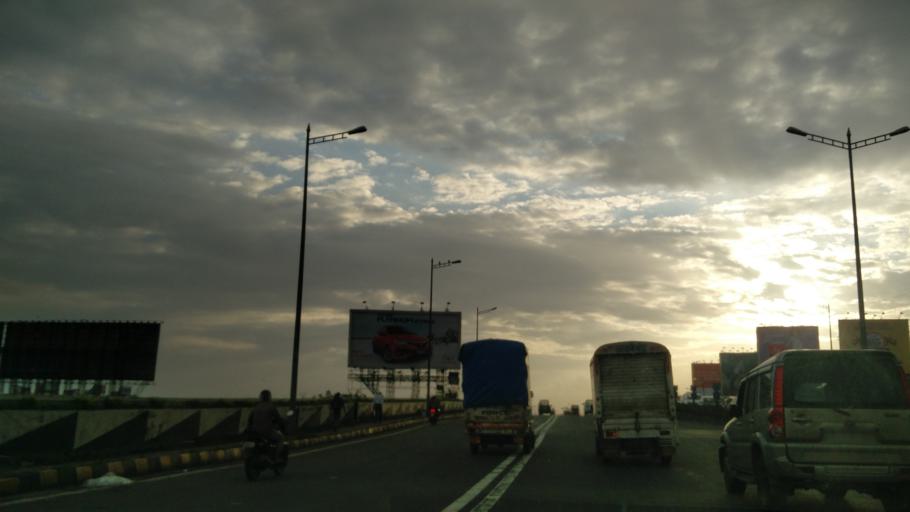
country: IN
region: Maharashtra
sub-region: Mumbai Suburban
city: Mumbai
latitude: 19.0518
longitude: 72.8431
